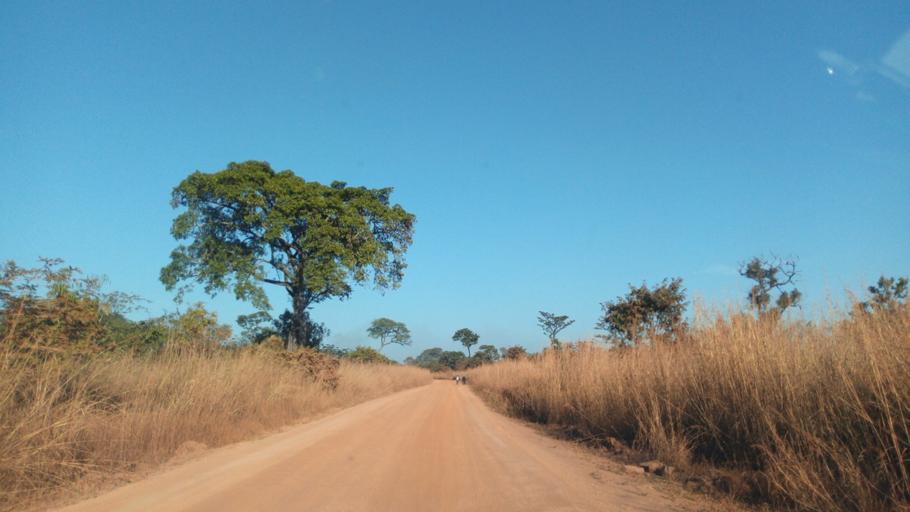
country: ZM
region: Luapula
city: Mwense
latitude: -10.4842
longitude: 28.5011
